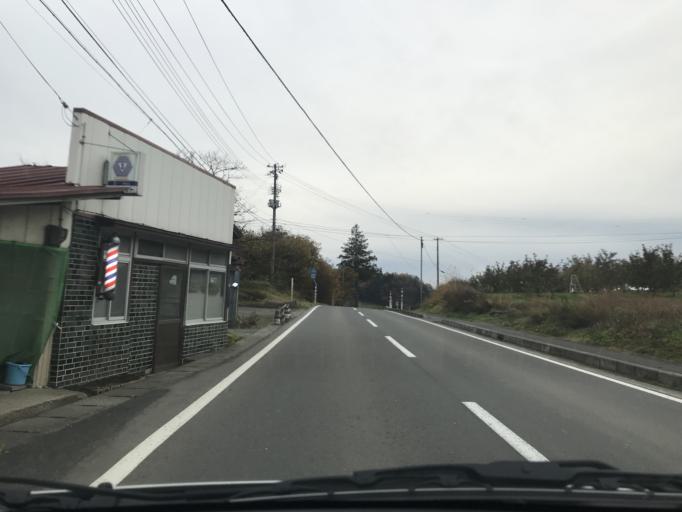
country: JP
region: Iwate
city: Kitakami
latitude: 39.2734
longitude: 141.2679
